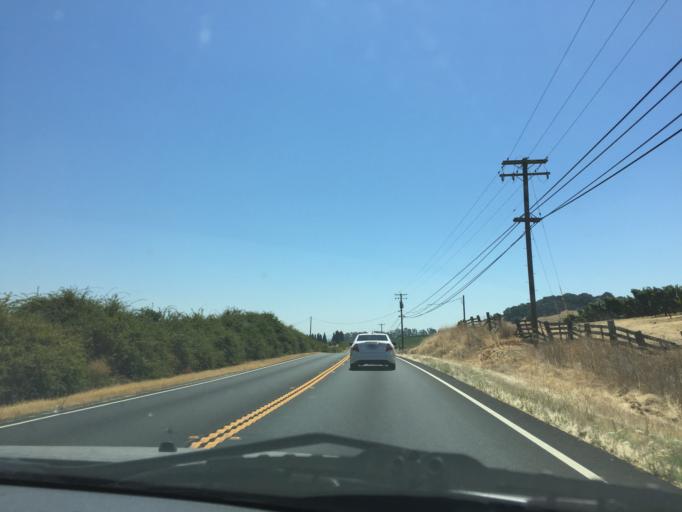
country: US
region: California
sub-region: Sonoma County
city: Temelec
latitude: 38.2068
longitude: -122.4524
